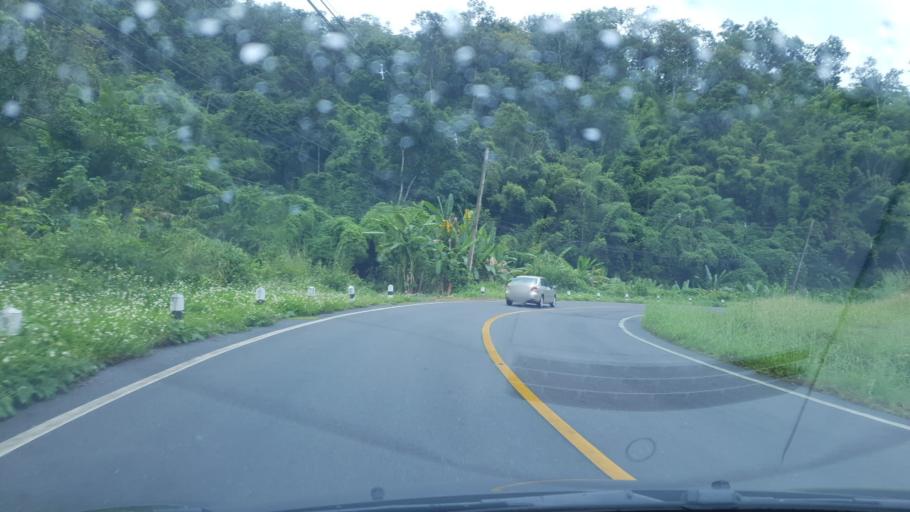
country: TH
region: Mae Hong Son
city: Mae La Noi
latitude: 18.5697
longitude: 97.9330
